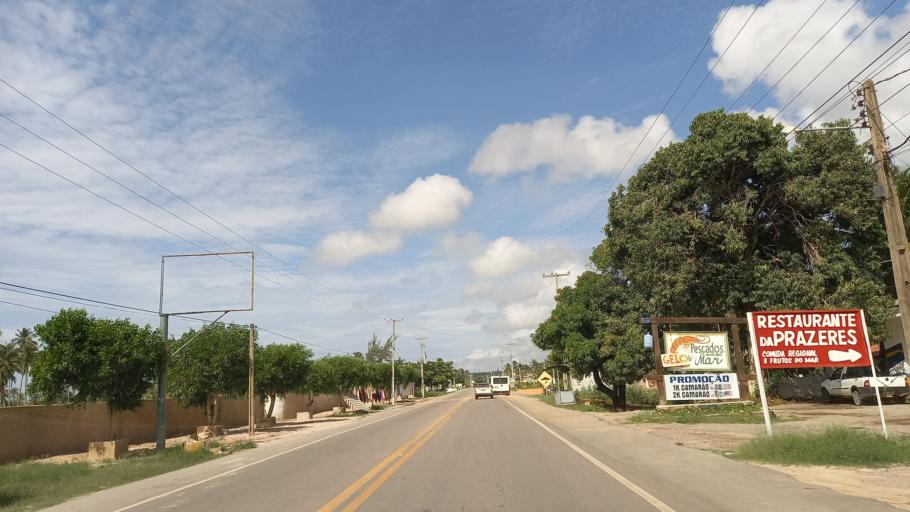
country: BR
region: Pernambuco
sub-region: Sao Jose Da Coroa Grande
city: Sao Jose da Coroa Grande
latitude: -8.9348
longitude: -35.1687
